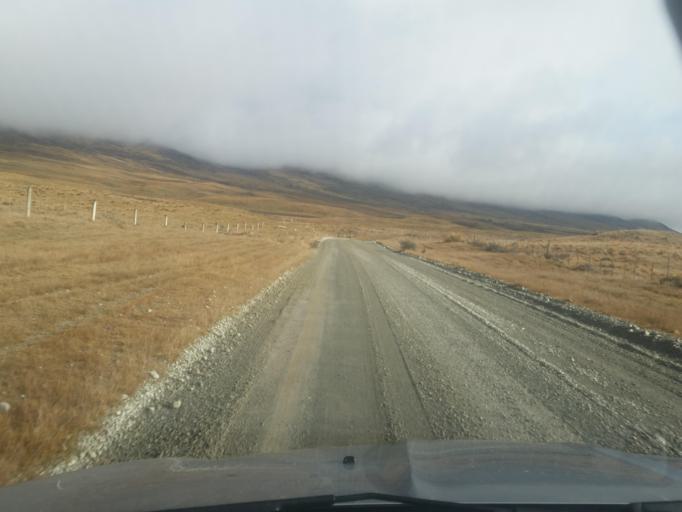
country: NZ
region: Canterbury
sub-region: Ashburton District
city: Methven
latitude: -43.6101
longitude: 171.0309
